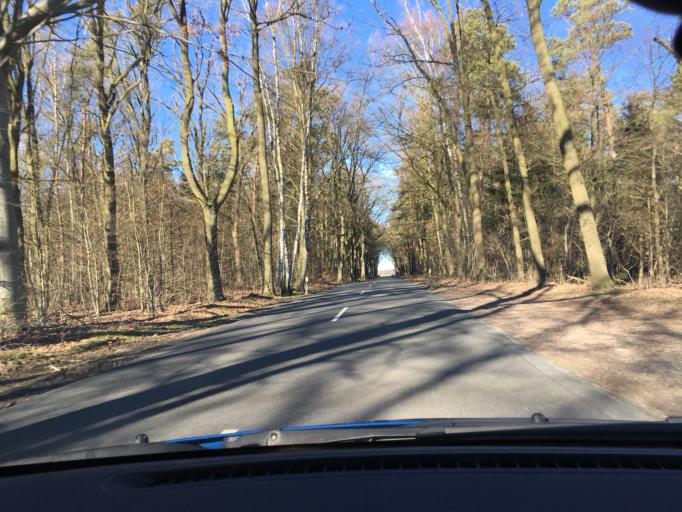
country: DE
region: Lower Saxony
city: Schwienau
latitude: 52.9855
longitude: 10.4450
